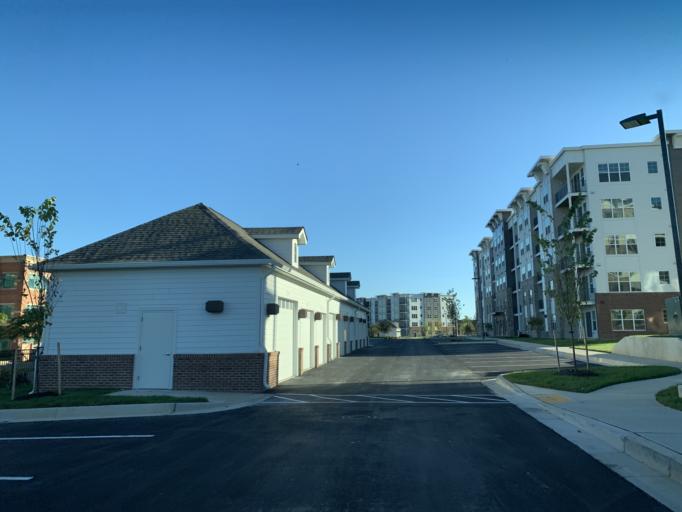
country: US
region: Maryland
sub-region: Baltimore County
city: Rossville
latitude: 39.3702
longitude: -76.4700
